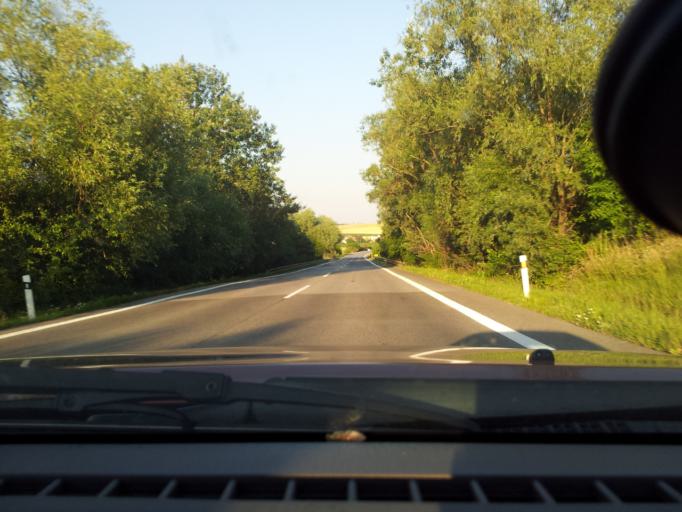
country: SK
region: Trnavsky
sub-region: Okres Skalica
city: Holic
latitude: 48.8032
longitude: 17.1853
